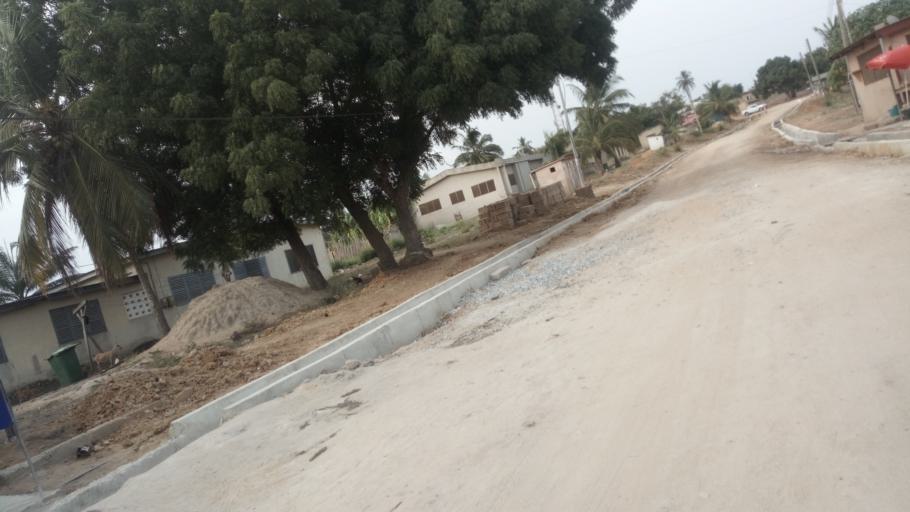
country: GH
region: Central
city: Winneba
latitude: 5.3559
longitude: -0.6280
